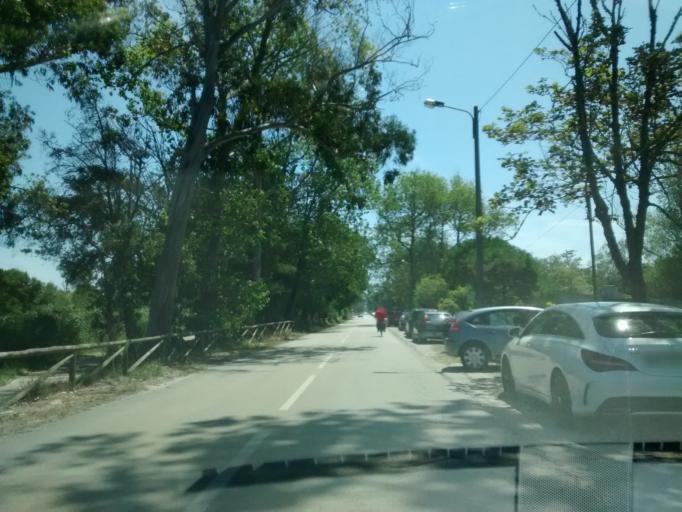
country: PT
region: Coimbra
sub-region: Mira
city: Mira
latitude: 40.4469
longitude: -8.7998
